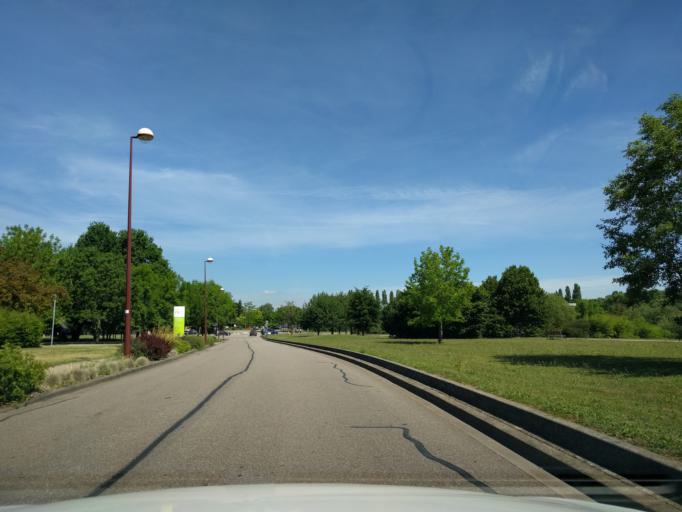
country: FR
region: Lorraine
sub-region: Departement de la Moselle
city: Peltre
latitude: 49.1036
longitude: 6.2156
